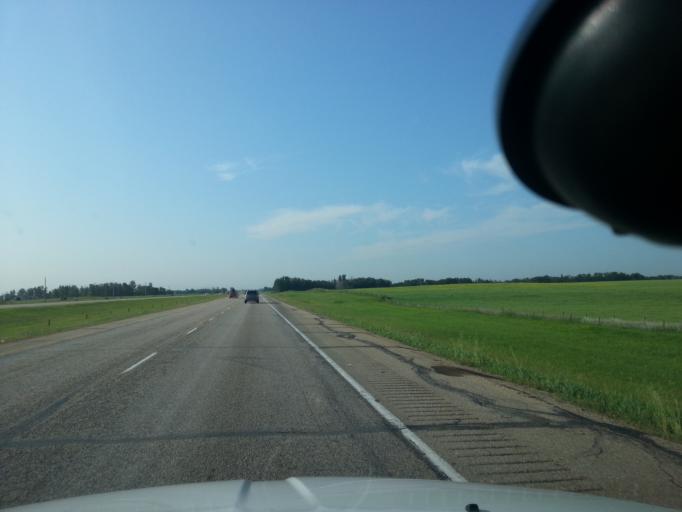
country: CA
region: Alberta
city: Ponoka
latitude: 52.8870
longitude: -113.6442
